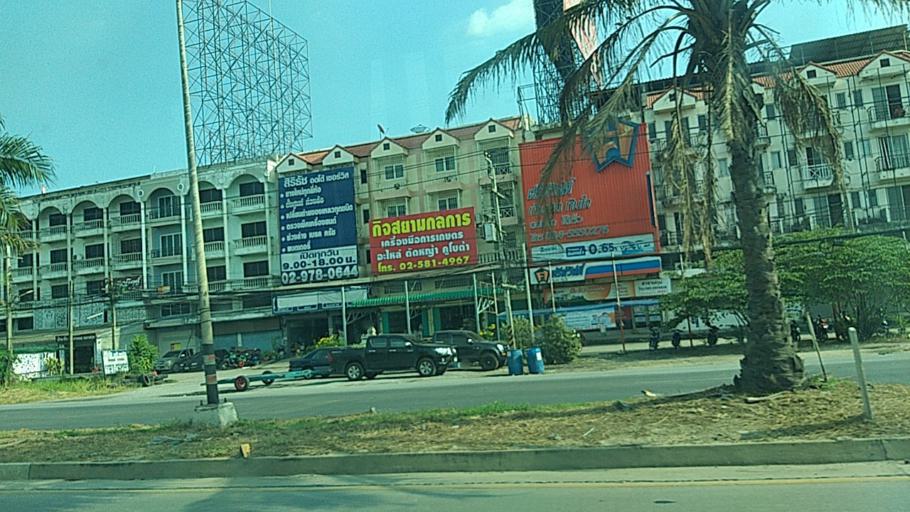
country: TH
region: Pathum Thani
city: Pathum Thani
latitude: 14.0300
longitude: 100.5318
